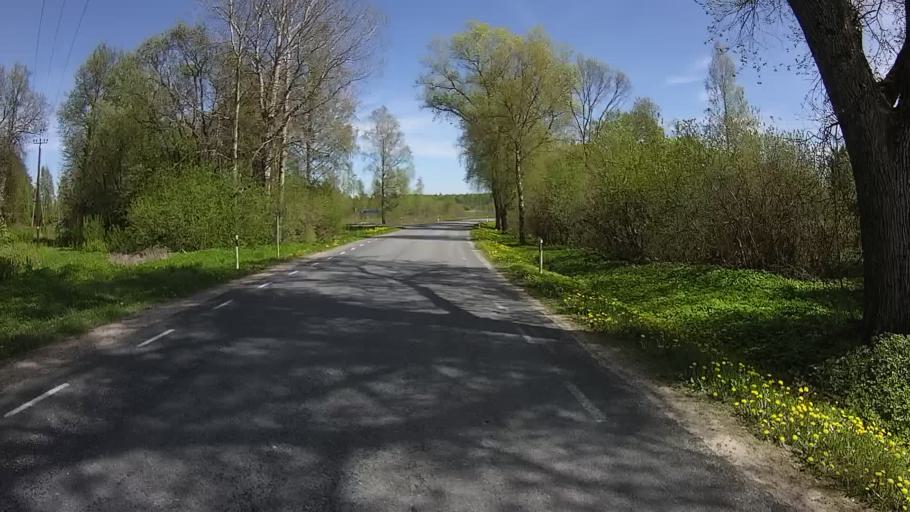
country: LV
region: Apes Novads
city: Ape
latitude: 57.6201
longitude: 26.5974
